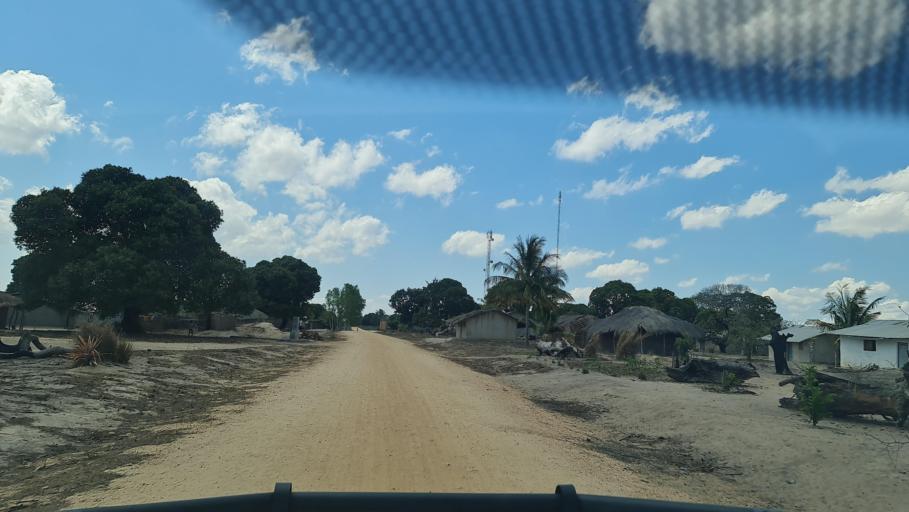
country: MZ
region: Nampula
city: Nacala
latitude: -14.1731
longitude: 40.2601
